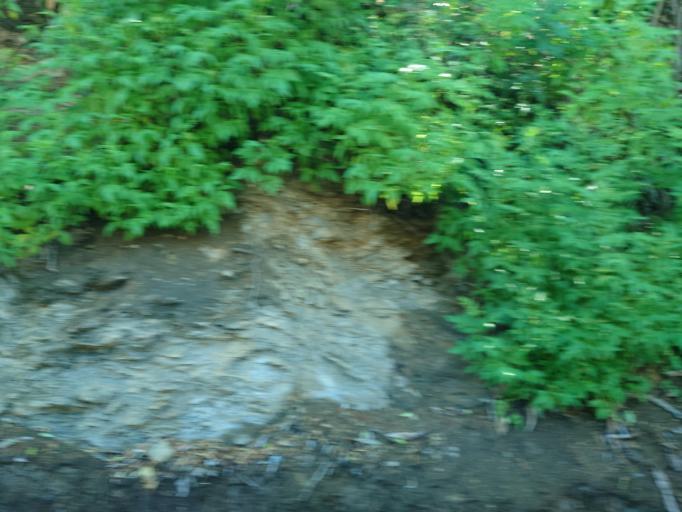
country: NC
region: South Province
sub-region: Noumea
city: Noumea
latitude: -22.2729
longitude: 166.4496
